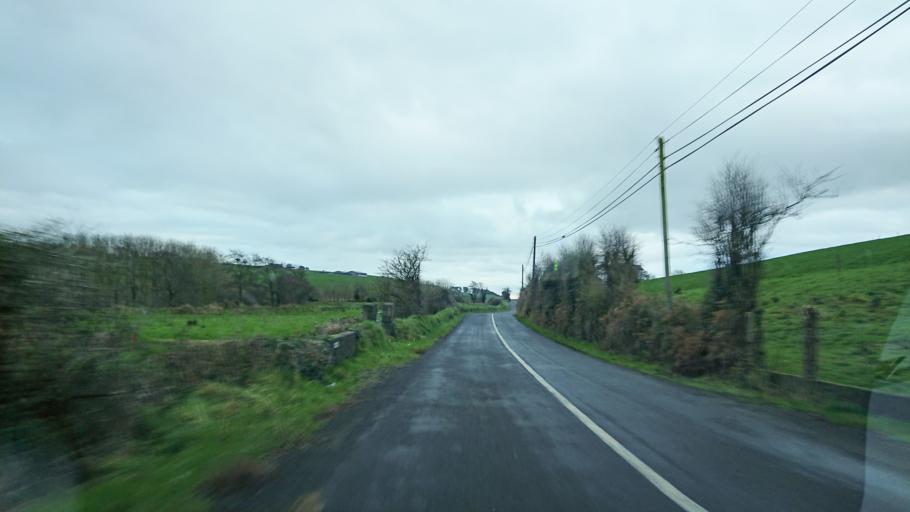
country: IE
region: Munster
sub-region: Waterford
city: Portlaw
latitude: 52.1533
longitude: -7.3820
